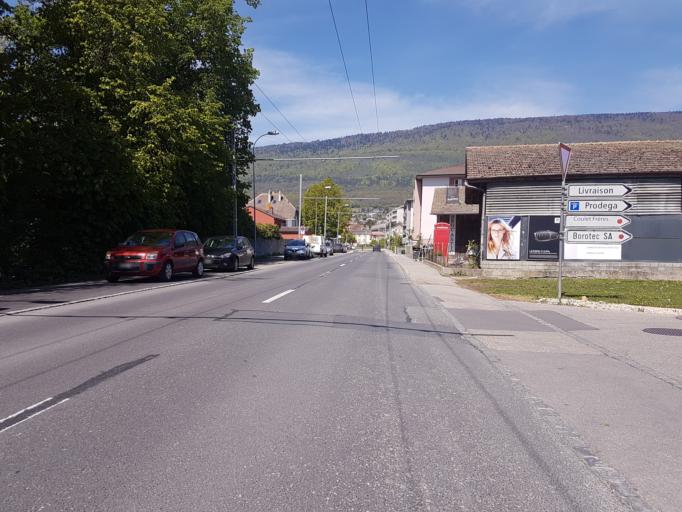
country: CH
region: Neuchatel
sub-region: Neuchatel District
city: Saint-Blaise
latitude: 47.0106
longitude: 6.9927
